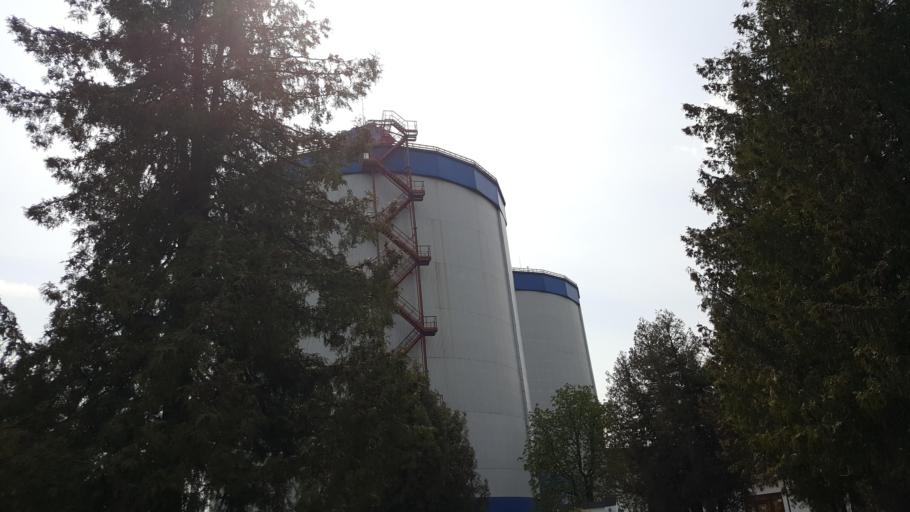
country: BY
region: Brest
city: Zhabinka
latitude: 52.1872
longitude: 23.9777
